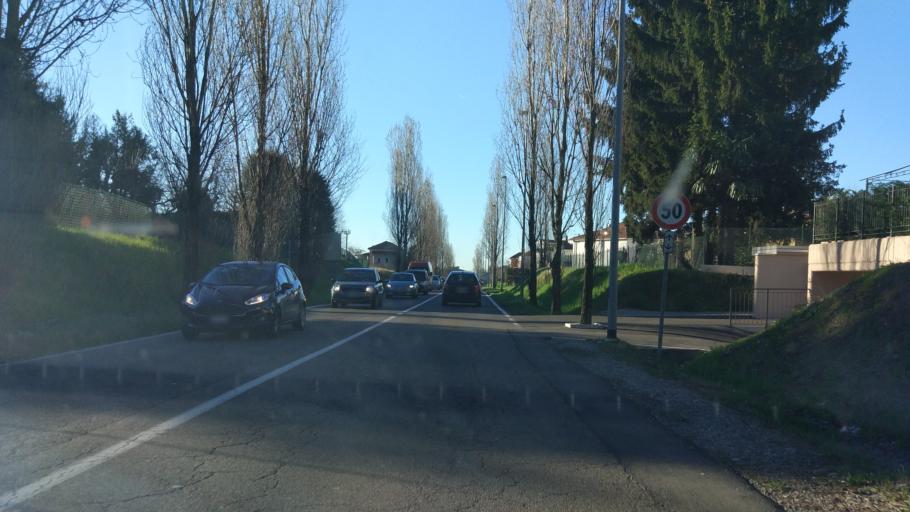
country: IT
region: Lombardy
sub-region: Provincia di Como
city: Arosio
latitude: 45.7063
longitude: 9.2154
